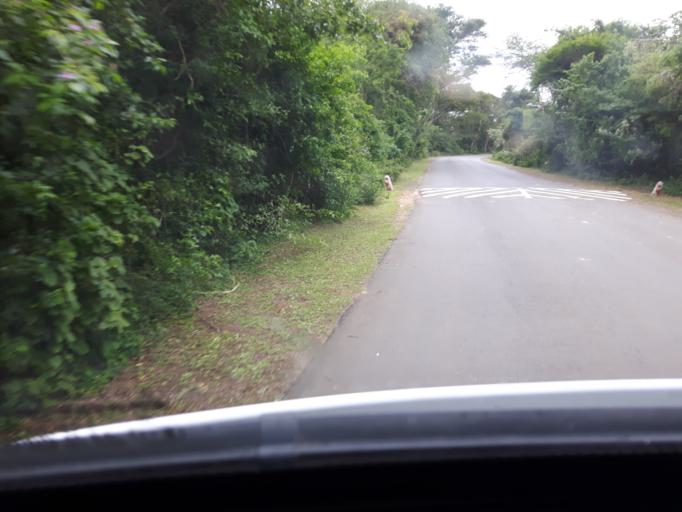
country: ZA
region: KwaZulu-Natal
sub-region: uMkhanyakude District Municipality
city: Mtubatuba
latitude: -28.3843
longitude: 32.4153
